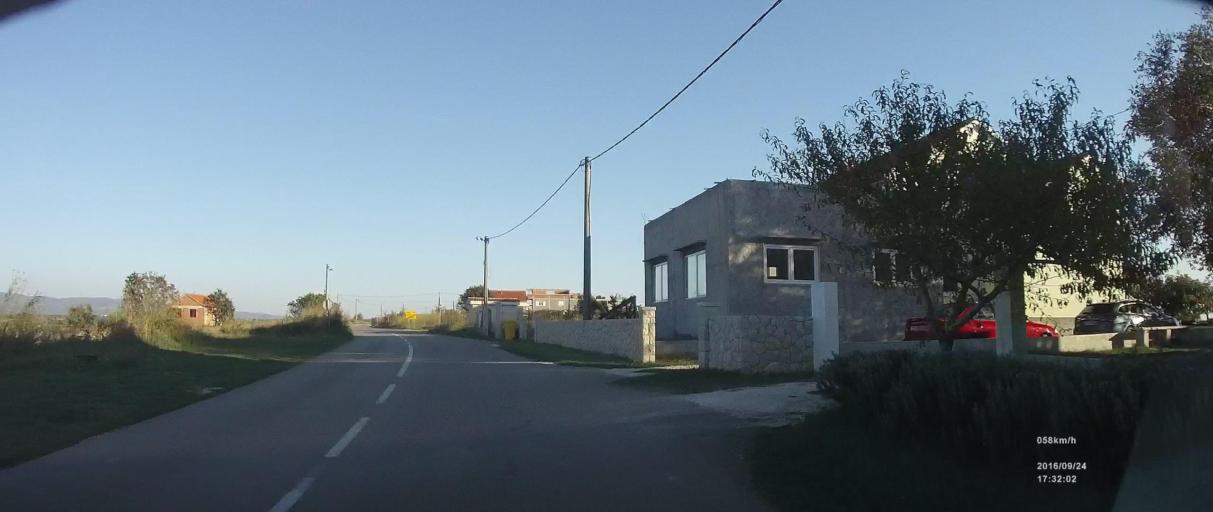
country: HR
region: Zadarska
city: Posedarje
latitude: 44.1849
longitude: 15.4469
